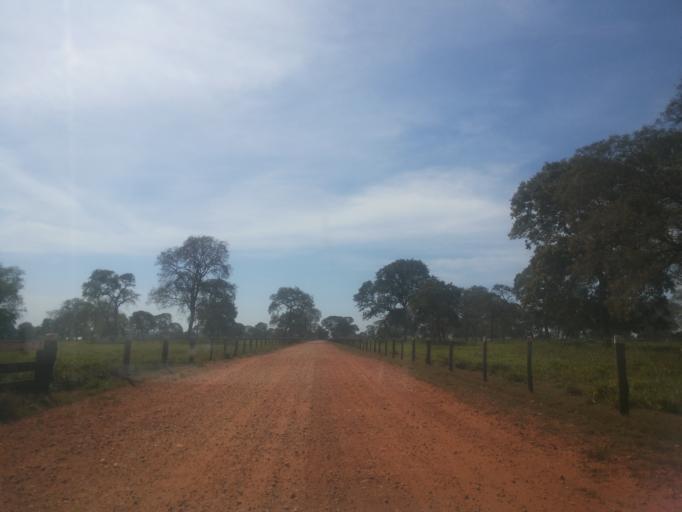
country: BR
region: Minas Gerais
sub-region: Santa Vitoria
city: Santa Vitoria
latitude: -19.0110
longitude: -50.4302
